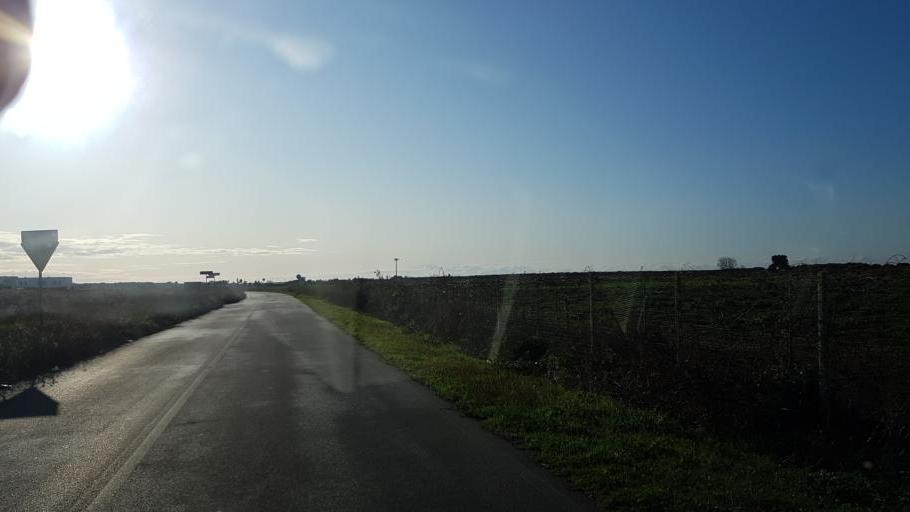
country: IT
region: Apulia
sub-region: Provincia di Brindisi
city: Torchiarolo
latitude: 40.5394
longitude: 18.0627
